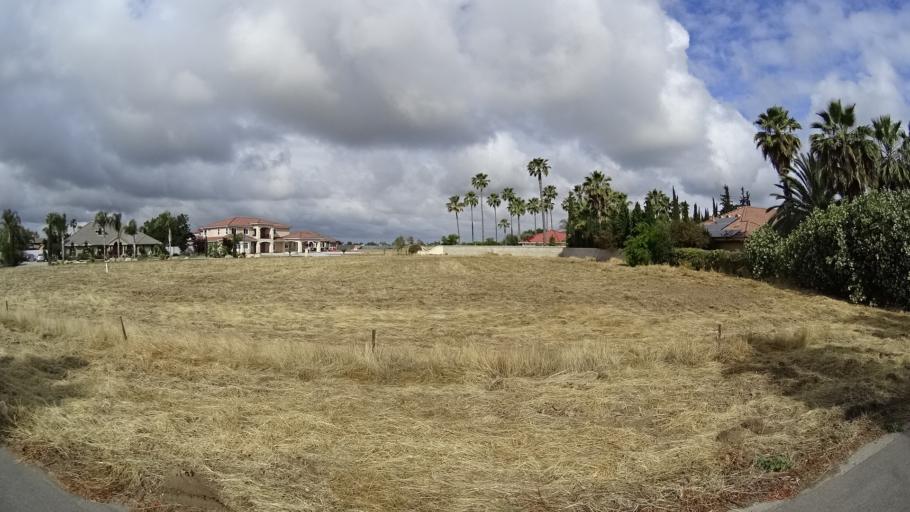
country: US
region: California
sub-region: Kings County
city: Lucerne
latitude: 36.3516
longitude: -119.6758
